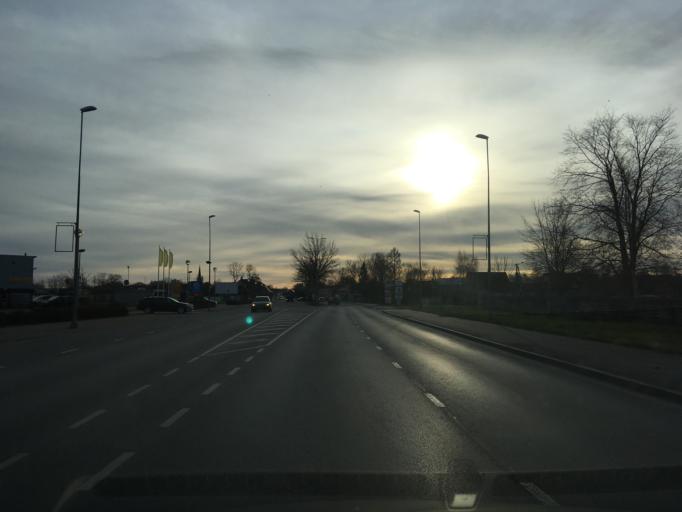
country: EE
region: Ida-Virumaa
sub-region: Johvi vald
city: Johvi
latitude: 59.3647
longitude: 27.3983
